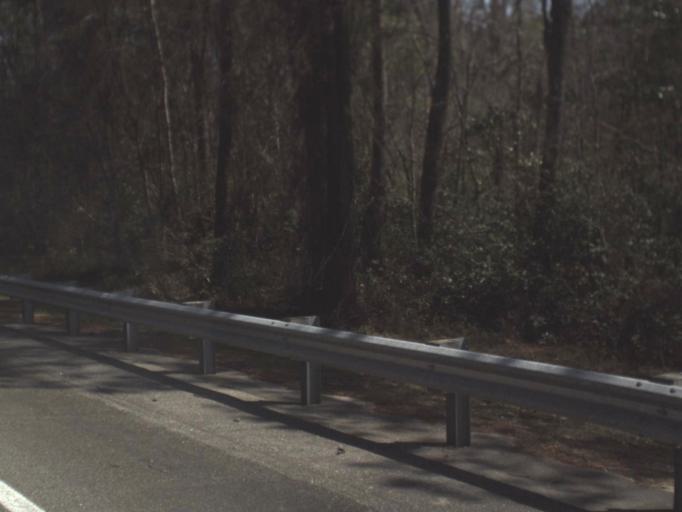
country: US
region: Florida
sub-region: Liberty County
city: Bristol
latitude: 30.5197
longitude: -84.8194
